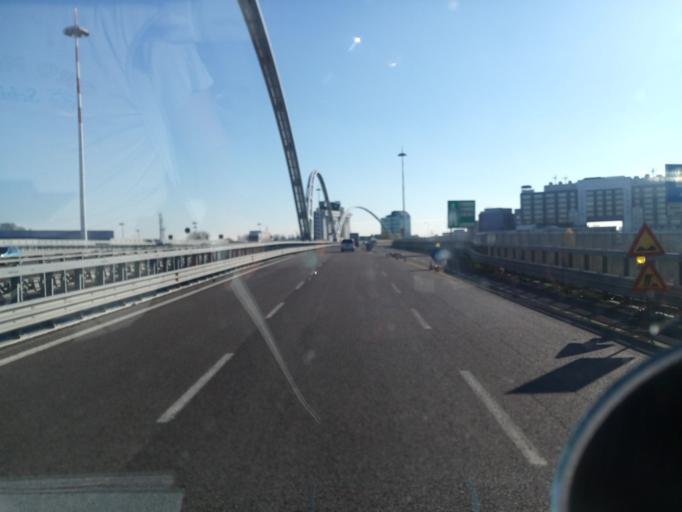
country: IT
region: Veneto
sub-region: Provincia di Padova
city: Noventa
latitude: 45.4194
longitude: 11.9293
